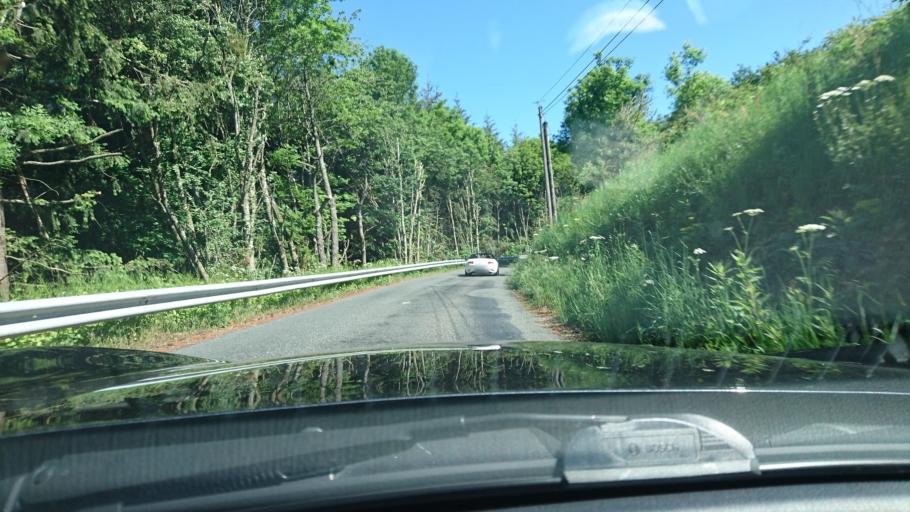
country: FR
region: Rhone-Alpes
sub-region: Departement de la Loire
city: Violay
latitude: 45.8468
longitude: 4.3633
